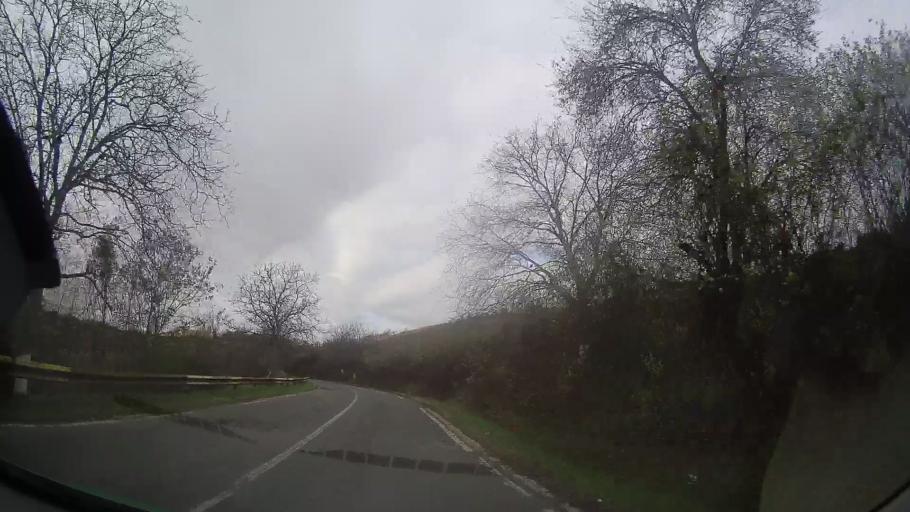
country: RO
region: Bistrita-Nasaud
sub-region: Comuna Silvasu de Campie
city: Silvasu de Campie
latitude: 46.7772
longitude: 24.3221
